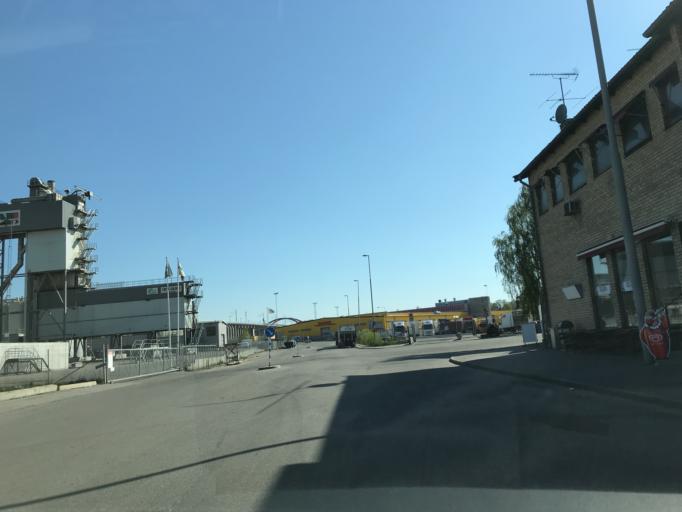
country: SE
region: Stockholm
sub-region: Stockholms Kommun
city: Arsta
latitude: 59.2971
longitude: 18.0197
